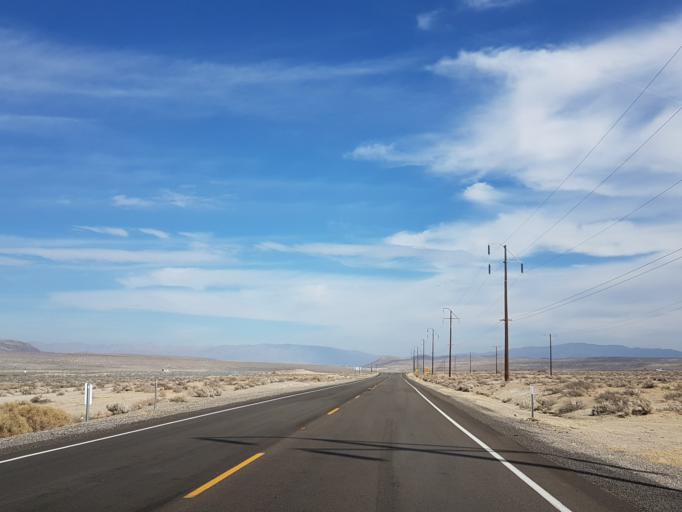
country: US
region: California
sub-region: Kern County
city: Ridgecrest
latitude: 35.6465
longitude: -117.5150
